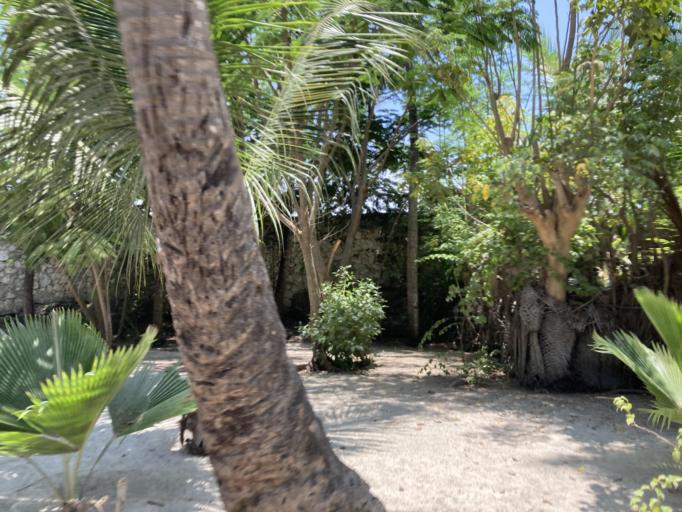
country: TZ
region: Zanzibar North
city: Gamba
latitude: -5.9254
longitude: 39.3577
